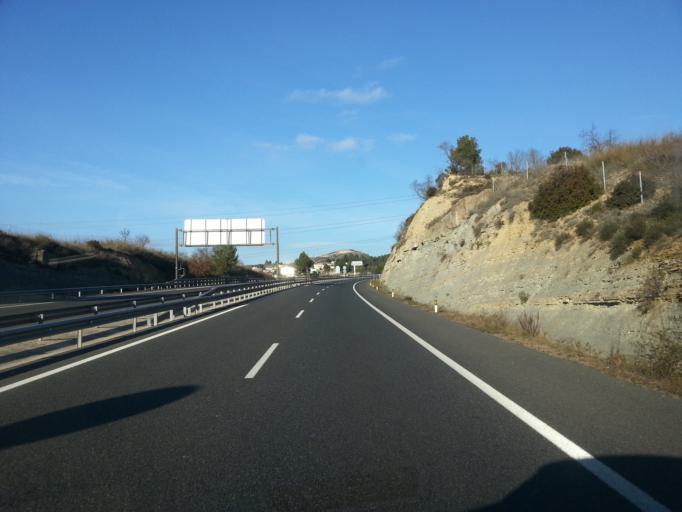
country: ES
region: Catalonia
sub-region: Provincia de Barcelona
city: Monistrol de Montserrat
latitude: 41.6552
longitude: 1.8676
